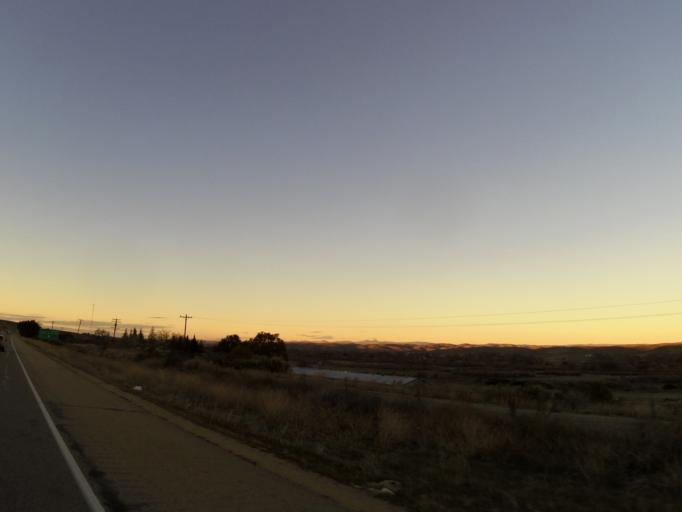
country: US
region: California
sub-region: San Luis Obispo County
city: Lake Nacimiento
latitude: 35.9704
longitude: -120.8956
